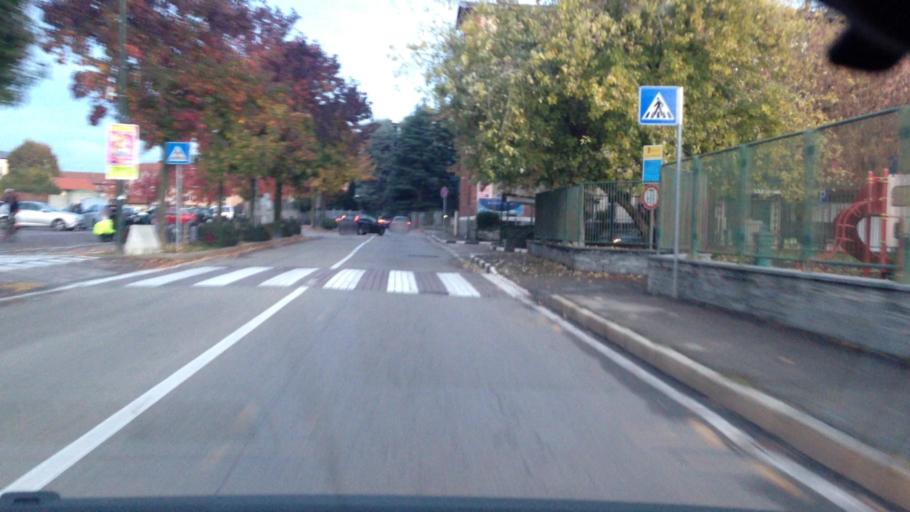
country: IT
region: Piedmont
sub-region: Provincia di Torino
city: Chieri
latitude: 45.0071
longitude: 7.8281
